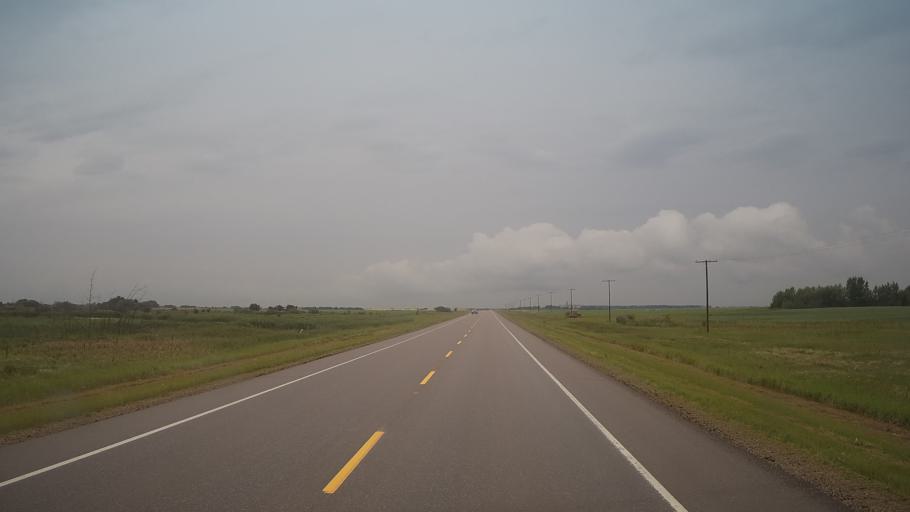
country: CA
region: Saskatchewan
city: Wilkie
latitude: 52.3191
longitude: -108.7008
